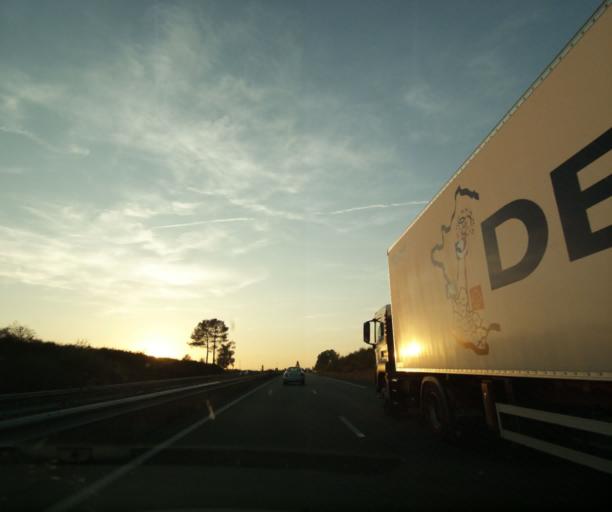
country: FR
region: Aquitaine
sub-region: Departement du Lot-et-Garonne
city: Meilhan-sur-Garonne
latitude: 44.4644
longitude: 0.0695
